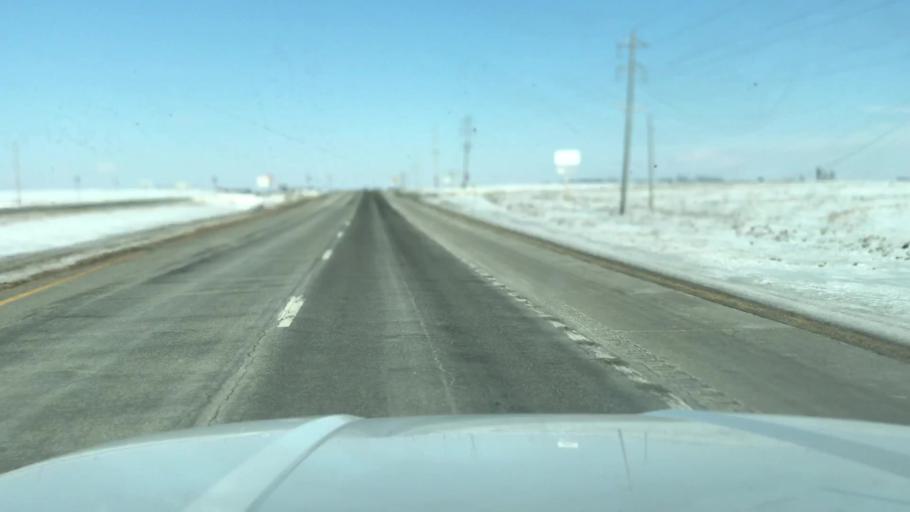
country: US
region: Missouri
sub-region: Nodaway County
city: Maryville
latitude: 40.2572
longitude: -94.8668
